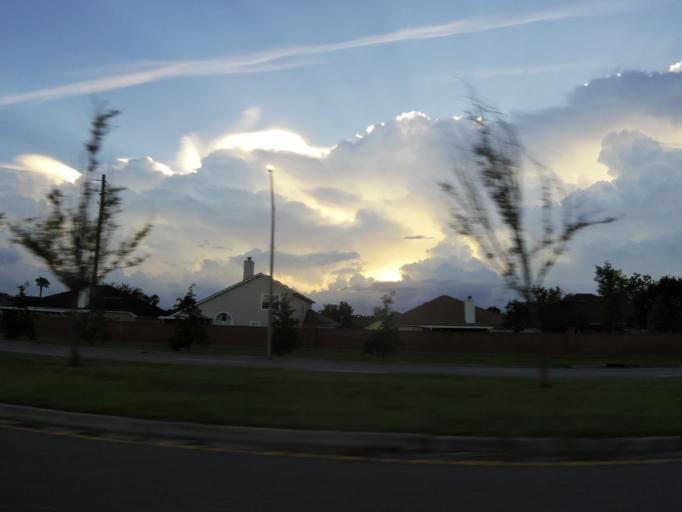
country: US
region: Florida
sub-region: Duval County
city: Neptune Beach
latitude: 30.2994
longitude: -81.4890
